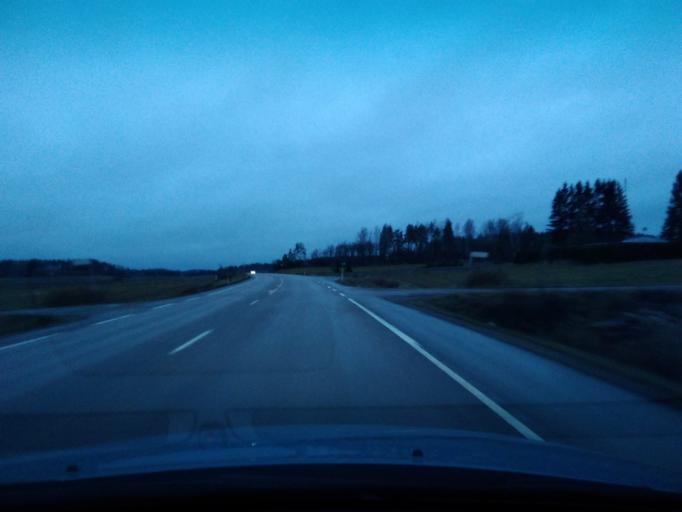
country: FI
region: Uusimaa
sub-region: Porvoo
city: Askola
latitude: 60.4756
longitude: 25.5683
